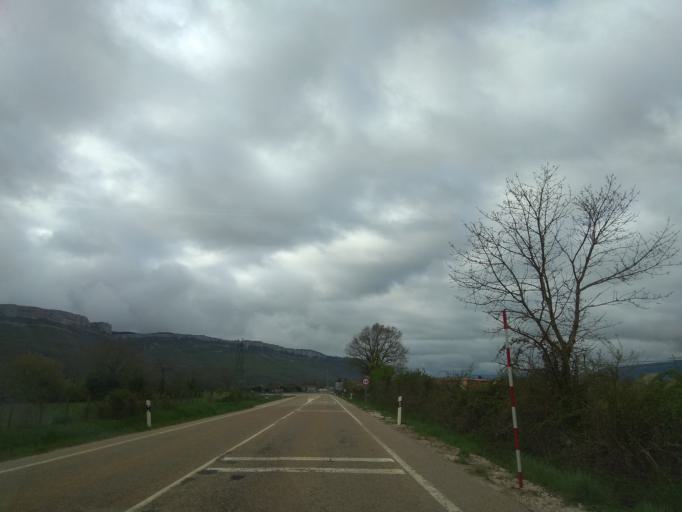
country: ES
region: Castille and Leon
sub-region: Provincia de Burgos
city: Espinosa de los Monteros
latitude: 43.0938
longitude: -3.4540
